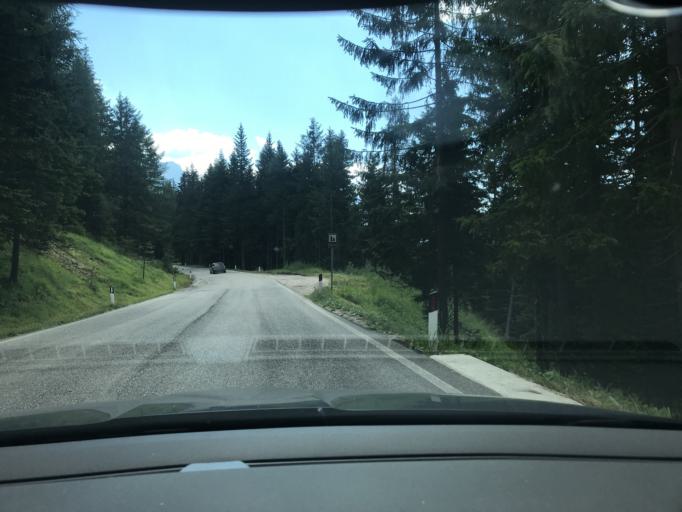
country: IT
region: Veneto
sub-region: Provincia di Belluno
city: Cortina d'Ampezzo
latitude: 46.5201
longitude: 12.0870
